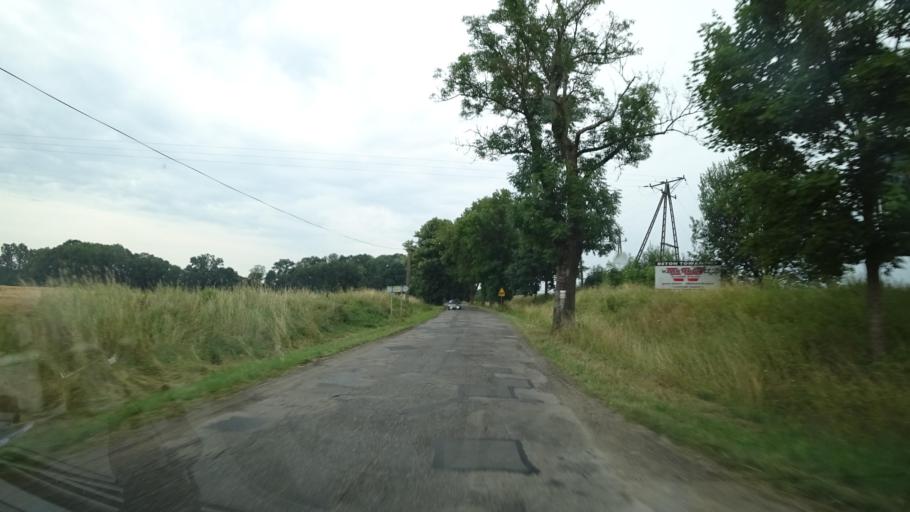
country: PL
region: Warmian-Masurian Voivodeship
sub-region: Powiat gizycki
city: Ryn
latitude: 53.9280
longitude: 21.5506
